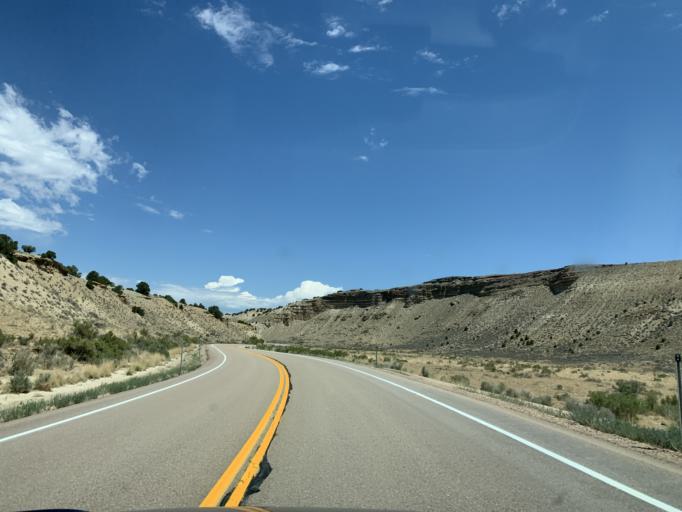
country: US
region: Utah
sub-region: Duchesne County
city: Duchesne
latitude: 39.9743
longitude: -110.1631
